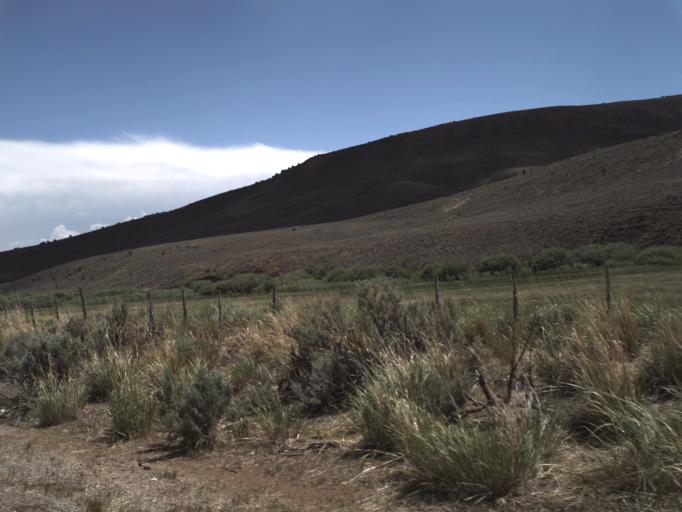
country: US
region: Utah
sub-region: Rich County
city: Randolph
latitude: 41.5022
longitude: -111.2835
